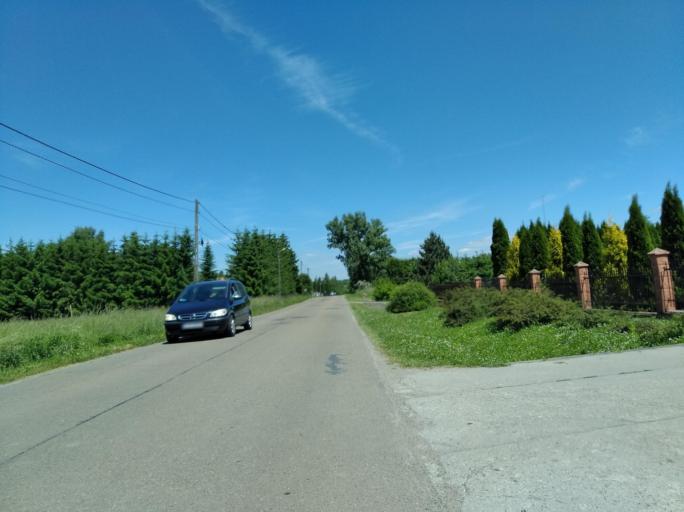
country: PL
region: Subcarpathian Voivodeship
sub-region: Powiat jasielski
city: Tarnowiec
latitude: 49.7234
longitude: 21.5633
